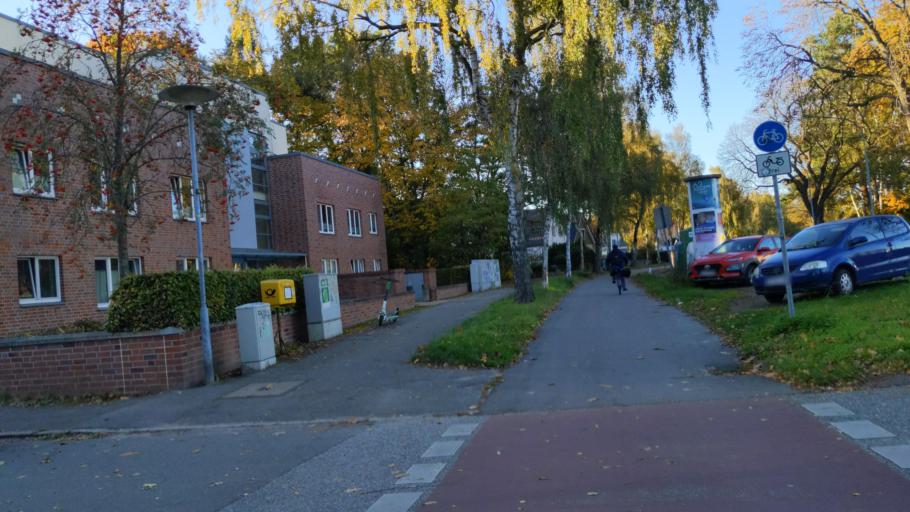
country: DE
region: Schleswig-Holstein
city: Gross Gronau
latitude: 53.8517
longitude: 10.7379
